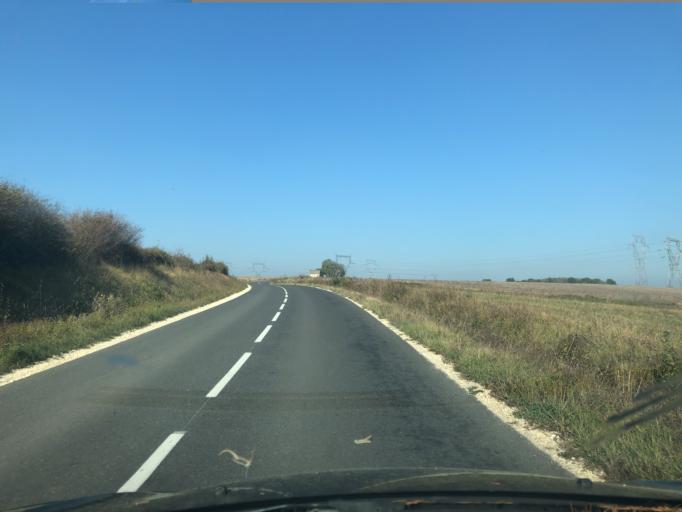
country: FR
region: Centre
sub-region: Departement d'Indre-et-Loire
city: Cerelles
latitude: 47.4884
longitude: 0.6607
